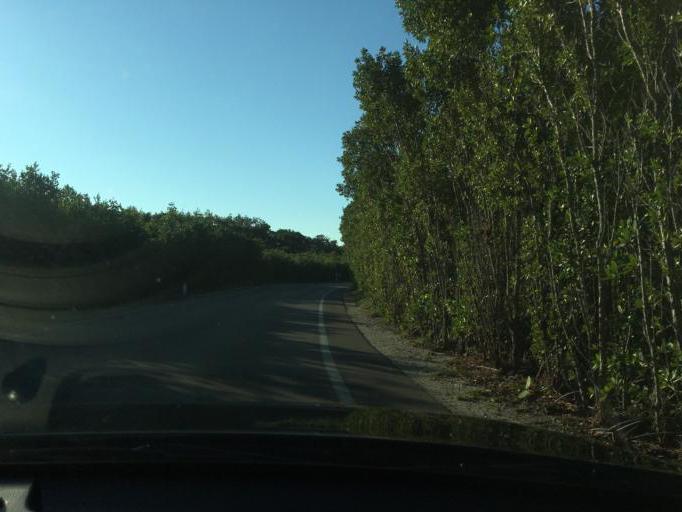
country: US
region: Florida
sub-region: Lee County
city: Pine Island Center
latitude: 26.5394
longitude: -82.1946
